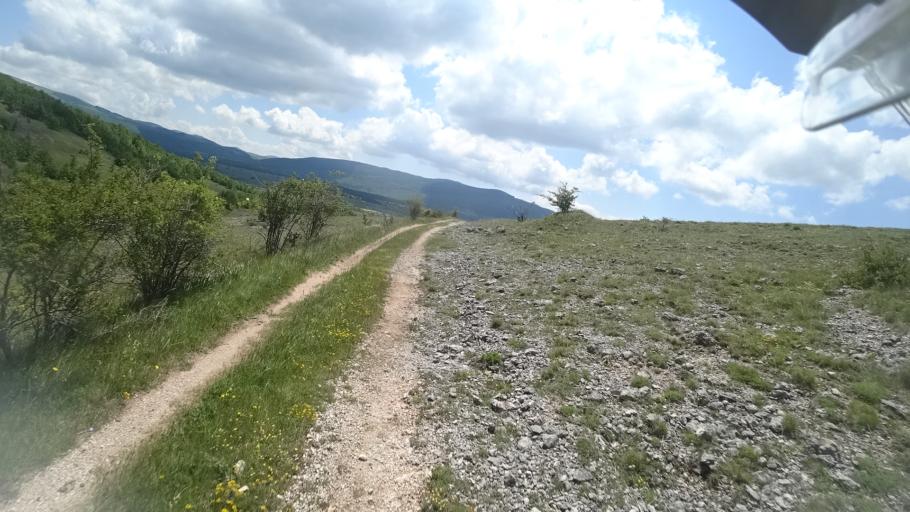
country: HR
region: Zadarska
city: Gracac
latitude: 44.3685
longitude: 15.9536
